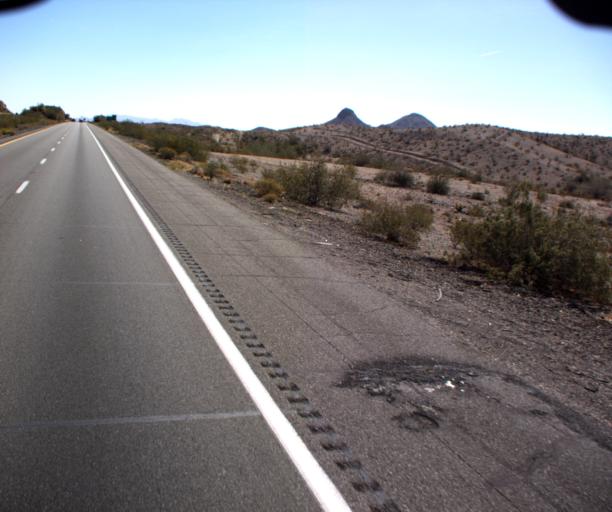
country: US
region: Arizona
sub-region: La Paz County
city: Quartzsite
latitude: 33.6472
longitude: -114.3439
